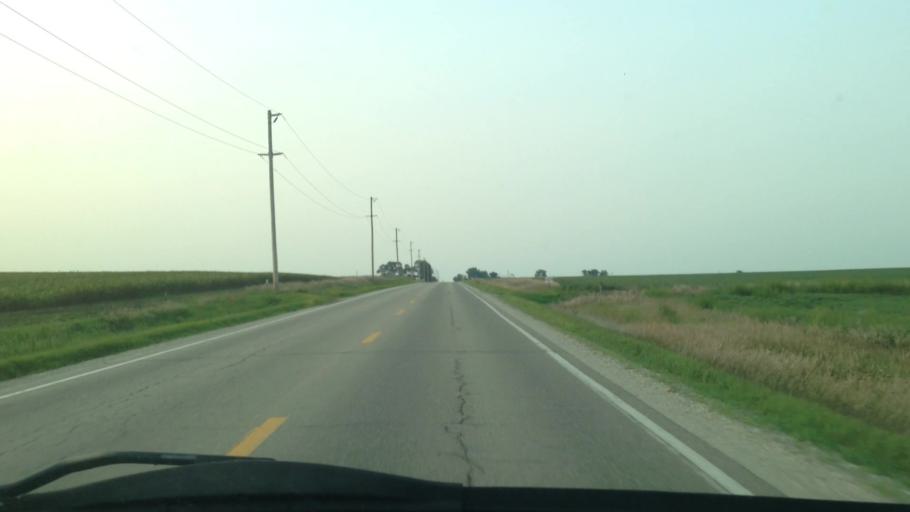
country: US
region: Iowa
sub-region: Iowa County
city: Marengo
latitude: 41.9560
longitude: -92.0852
